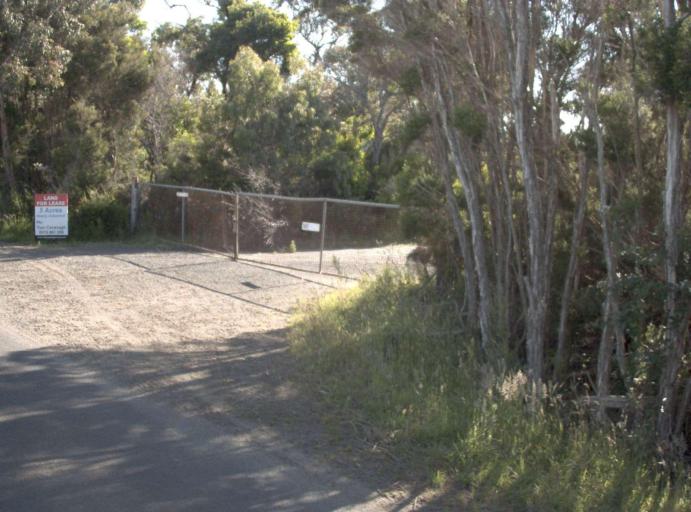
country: AU
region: Victoria
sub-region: Latrobe
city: Morwell
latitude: -38.7067
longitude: 146.3975
